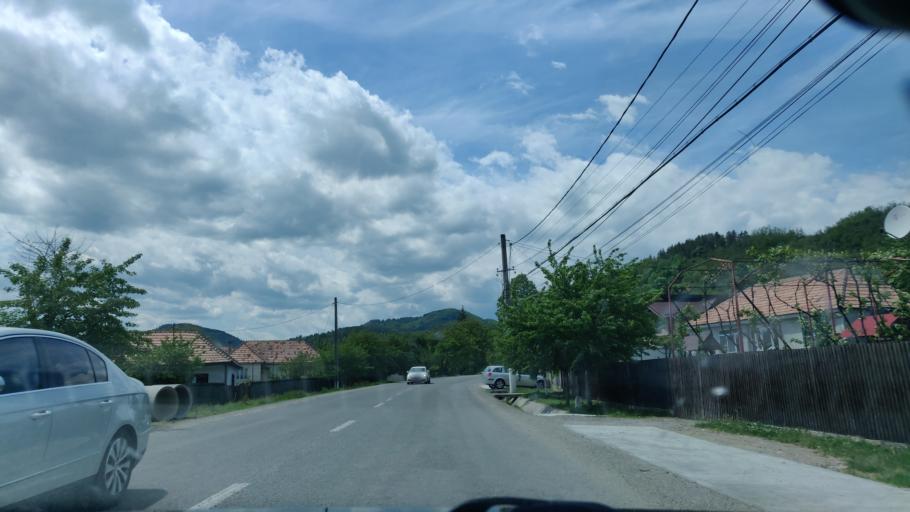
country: RO
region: Vrancea
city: Matacina
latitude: 45.8892
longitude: 26.8248
